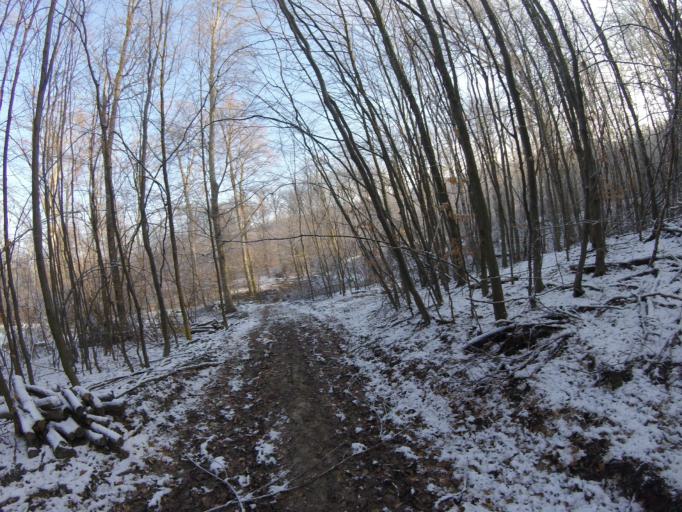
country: HU
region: Komarom-Esztergom
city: Pilismarot
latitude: 47.7300
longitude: 18.8617
